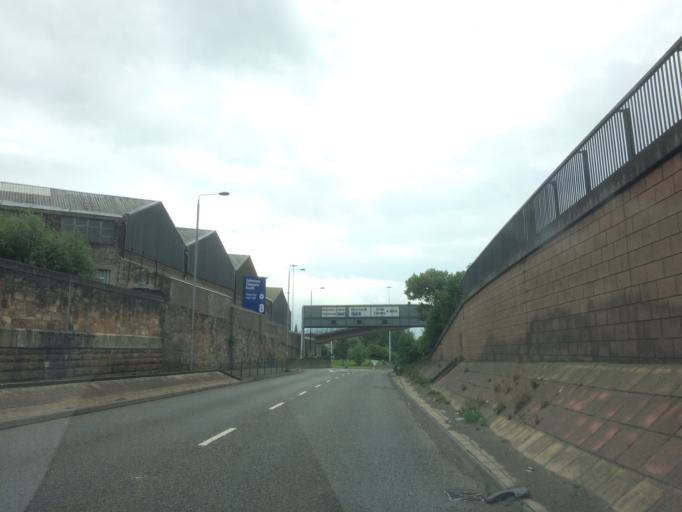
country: GB
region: Scotland
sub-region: Glasgow City
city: Glasgow
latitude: 55.8713
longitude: -4.2337
